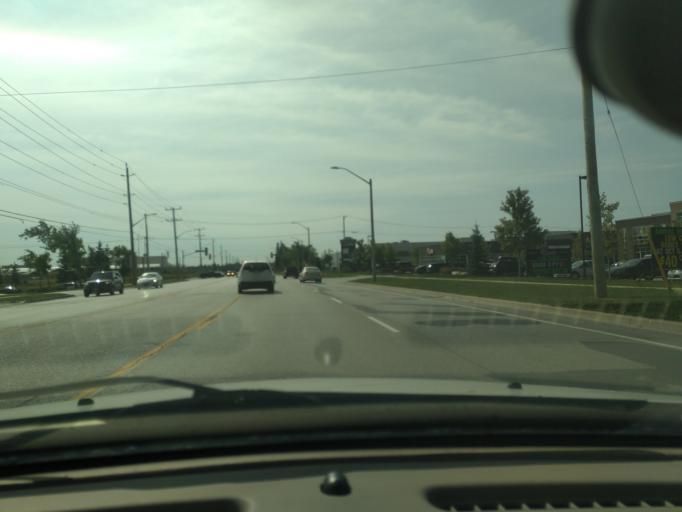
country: CA
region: Ontario
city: Innisfil
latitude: 44.3382
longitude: -79.7004
